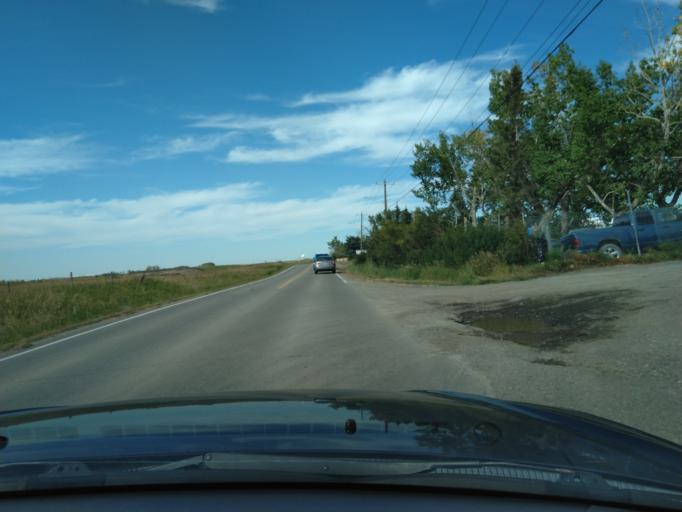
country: CA
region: Alberta
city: Calgary
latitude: 51.1172
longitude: -113.9817
